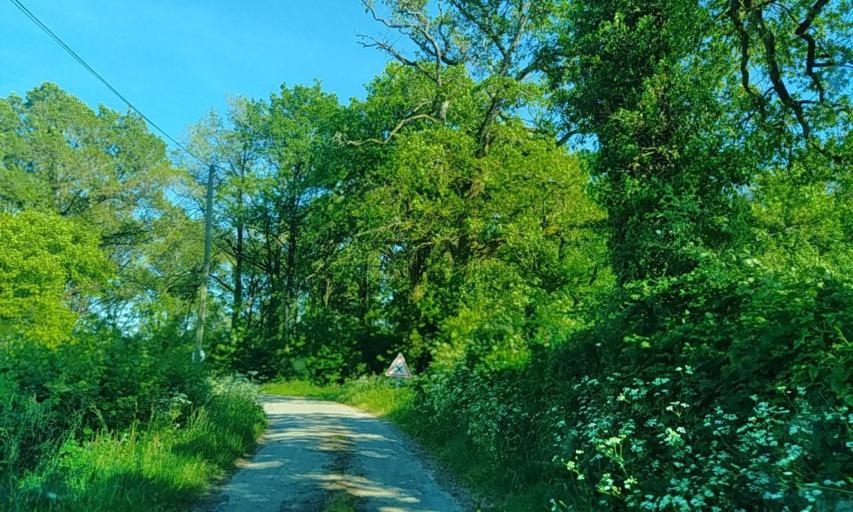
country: FR
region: Poitou-Charentes
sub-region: Departement des Deux-Sevres
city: Boisme
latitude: 46.7883
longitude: -0.4334
